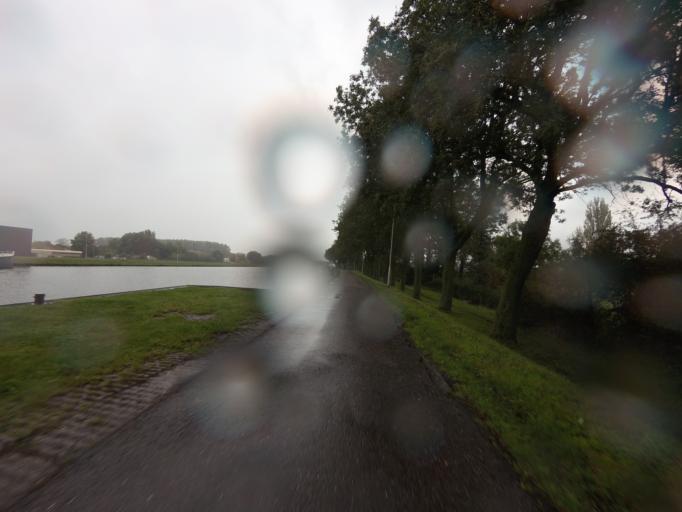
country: NL
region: South Holland
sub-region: Gemeente Gorinchem
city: Gorinchem
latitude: 51.8419
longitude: 4.9785
